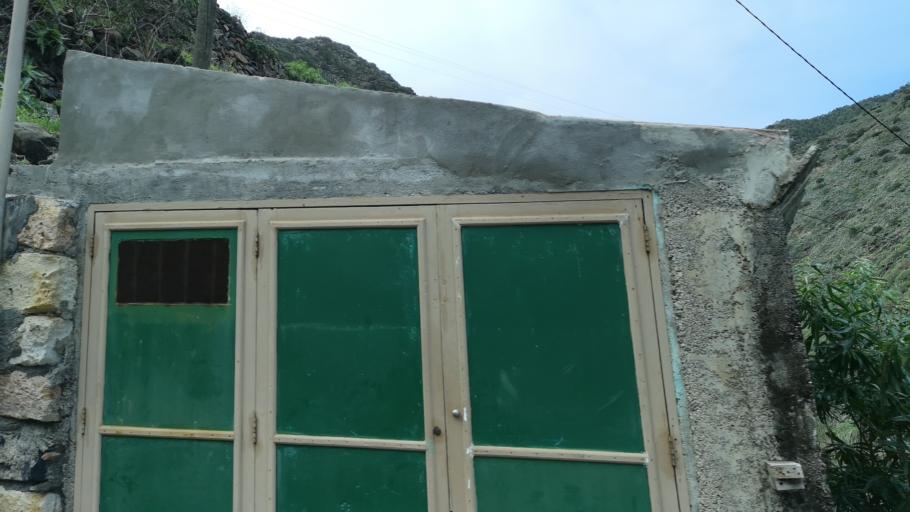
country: ES
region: Canary Islands
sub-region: Provincia de Santa Cruz de Tenerife
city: Vallehermosa
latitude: 28.1984
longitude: -17.2563
